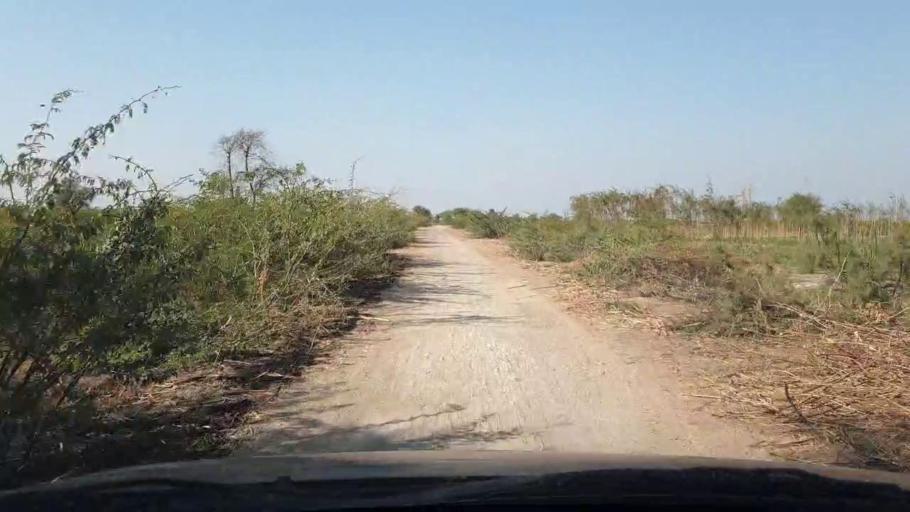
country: PK
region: Sindh
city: Samaro
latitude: 25.1736
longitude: 69.2843
